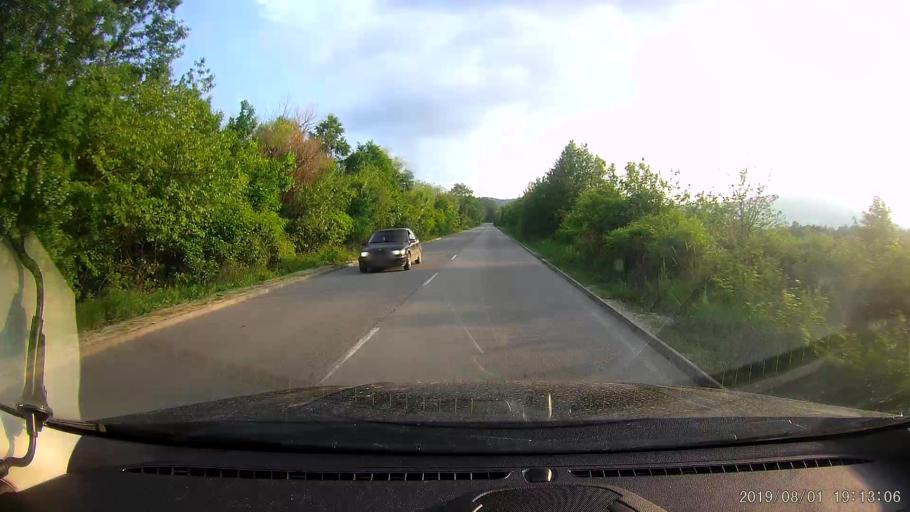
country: BG
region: Shumen
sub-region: Obshtina Smyadovo
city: Smyadovo
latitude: 42.9556
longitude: 26.9439
